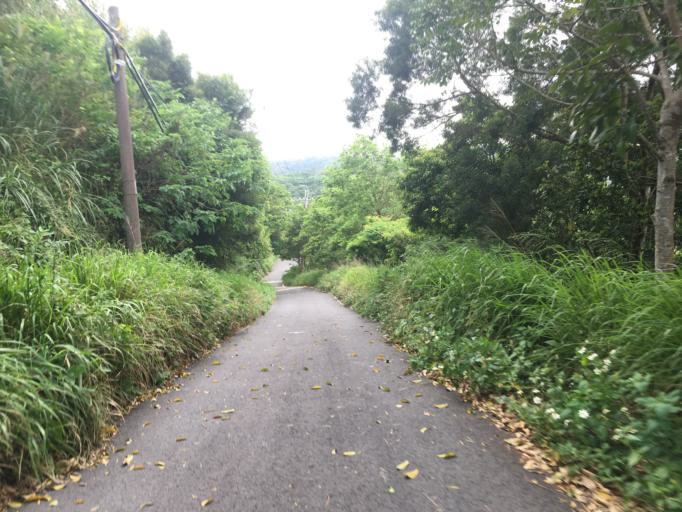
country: TW
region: Taiwan
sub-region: Hsinchu
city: Hsinchu
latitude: 24.7404
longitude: 120.9829
